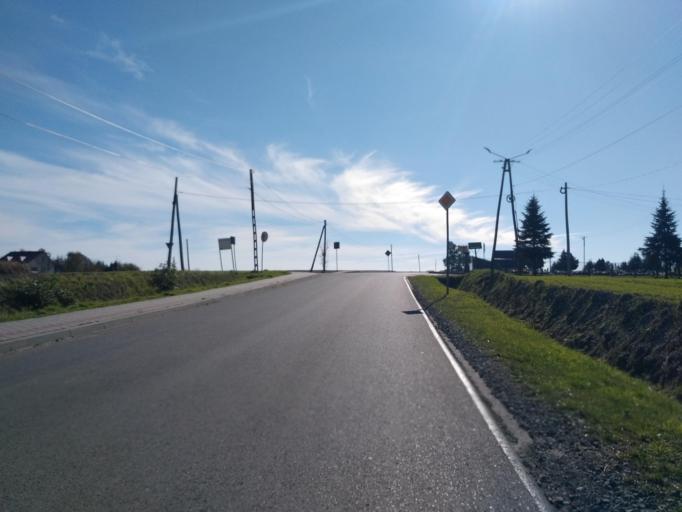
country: PL
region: Subcarpathian Voivodeship
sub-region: Powiat ropczycko-sedziszowski
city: Iwierzyce
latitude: 50.0235
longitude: 21.7690
